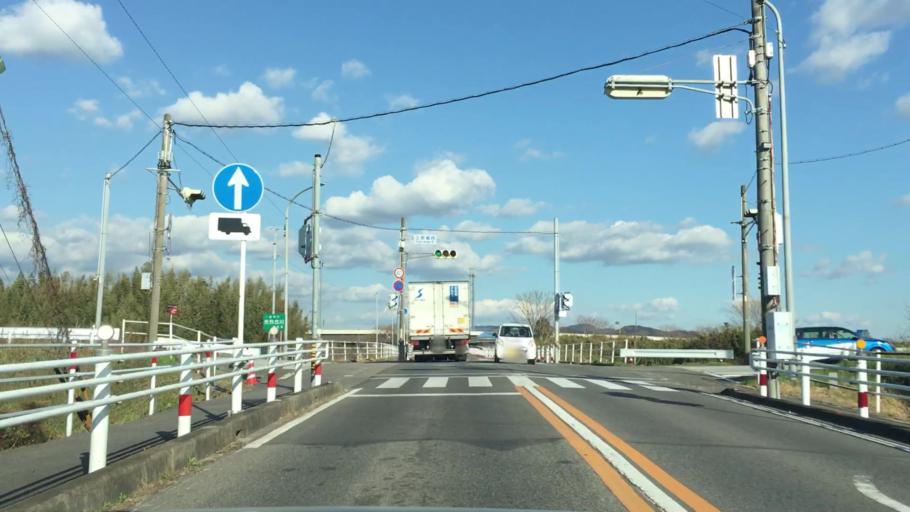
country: JP
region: Aichi
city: Nishio
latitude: 34.8729
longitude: 137.0792
